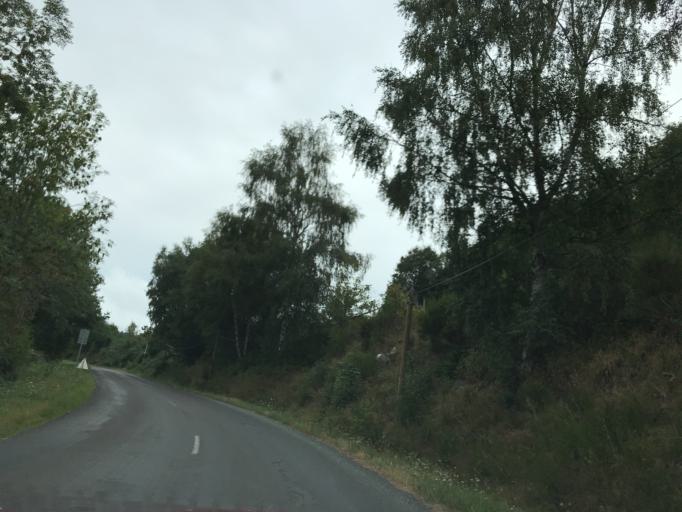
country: FR
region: Rhone-Alpes
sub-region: Departement de la Loire
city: Sail-sous-Couzan
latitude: 45.6975
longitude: 3.8499
